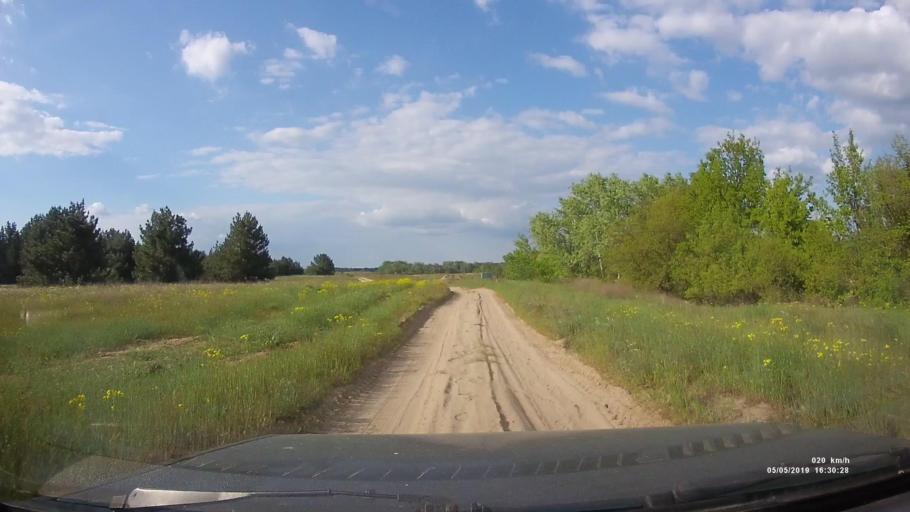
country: RU
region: Rostov
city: Ust'-Donetskiy
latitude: 47.7736
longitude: 41.0157
